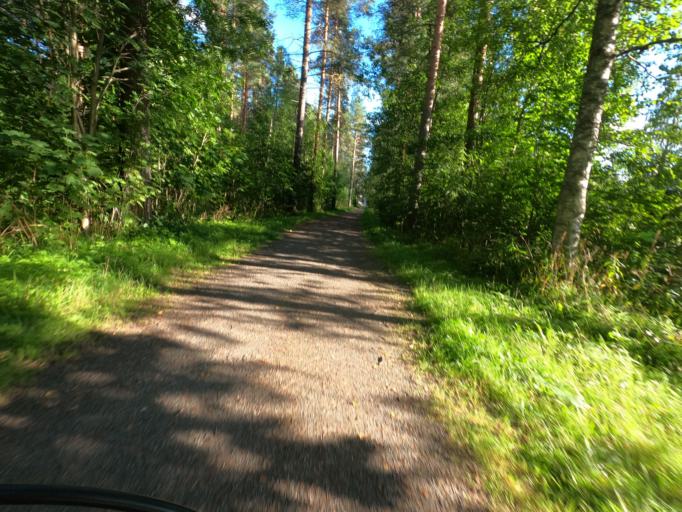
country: FI
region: North Karelia
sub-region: Joensuu
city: Joensuu
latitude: 62.6138
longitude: 29.7582
